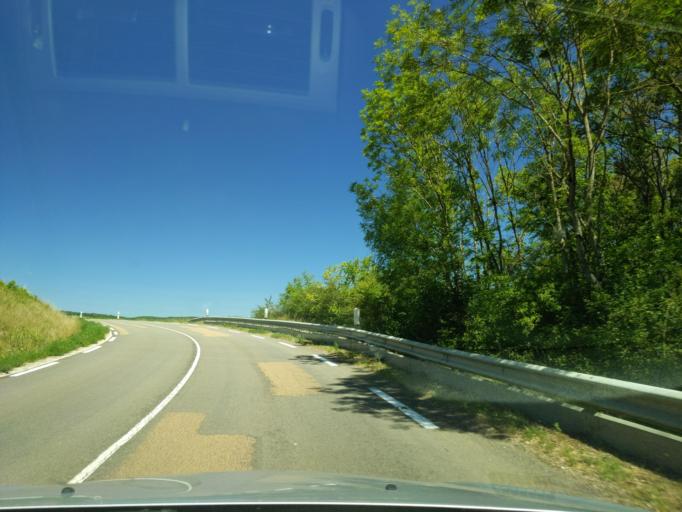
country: FR
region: Bourgogne
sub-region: Departement de la Cote-d'Or
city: Is-sur-Tille
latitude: 47.5105
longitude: 5.0750
